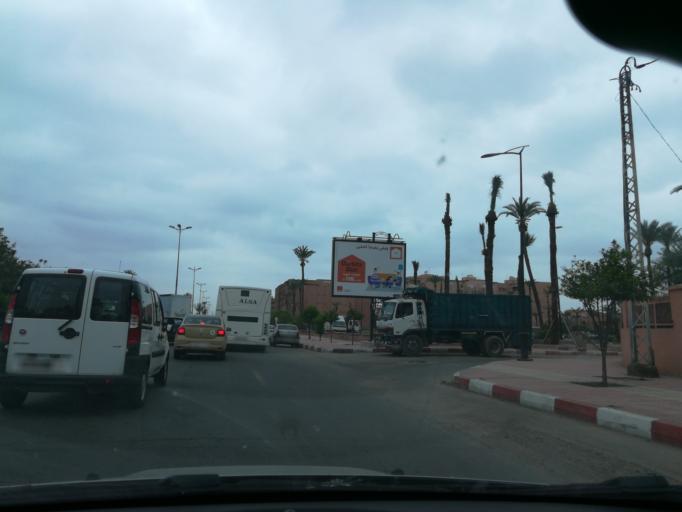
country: MA
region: Marrakech-Tensift-Al Haouz
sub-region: Marrakech
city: Marrakesh
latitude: 31.6408
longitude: -8.0058
